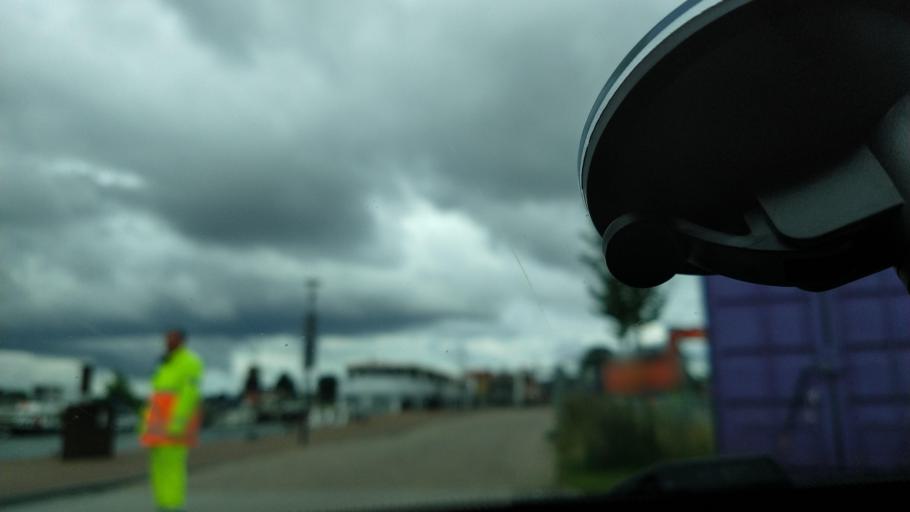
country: NL
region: Gelderland
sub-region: Gemeente Harderwijk
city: Harderwijk
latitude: 52.3545
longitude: 5.6198
